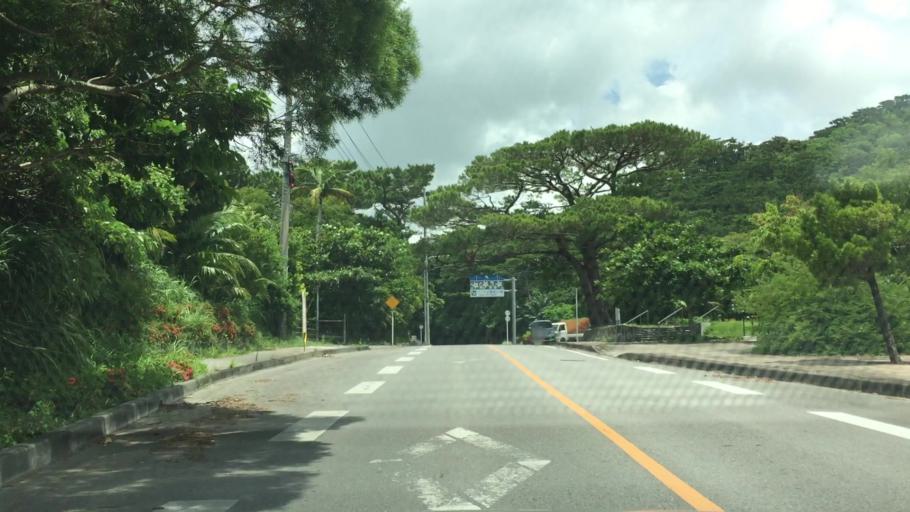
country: JP
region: Okinawa
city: Ishigaki
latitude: 24.3678
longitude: 124.1572
